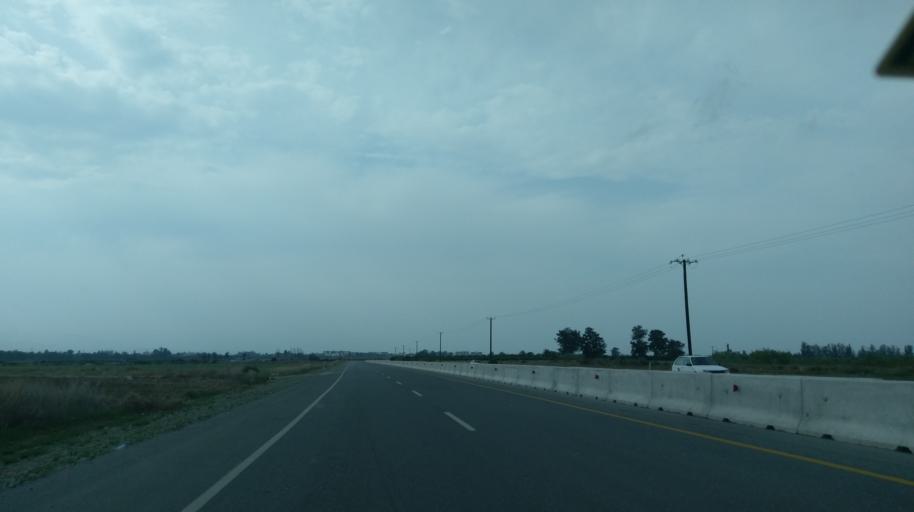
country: CY
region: Lefkosia
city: Morfou
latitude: 35.1997
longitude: 33.0279
